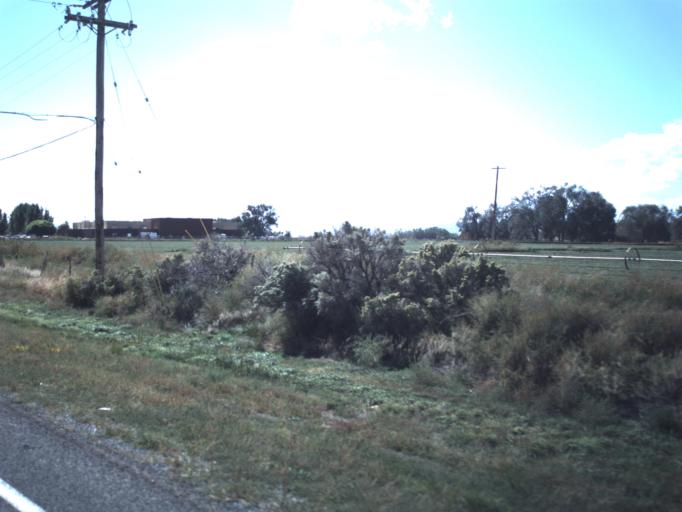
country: US
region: Utah
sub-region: Iron County
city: Enoch
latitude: 37.7508
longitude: -113.0553
